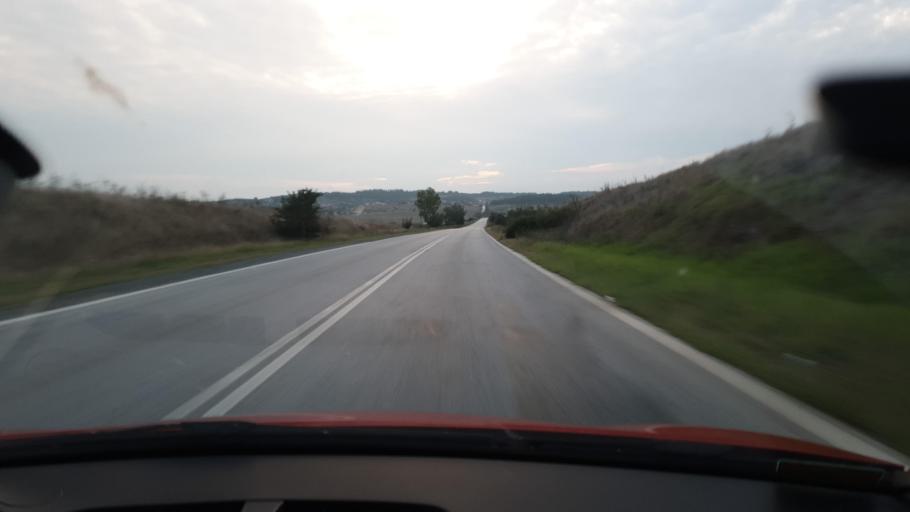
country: GR
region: Central Macedonia
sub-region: Nomos Kilkis
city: Kristoni
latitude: 40.9951
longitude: 22.7531
